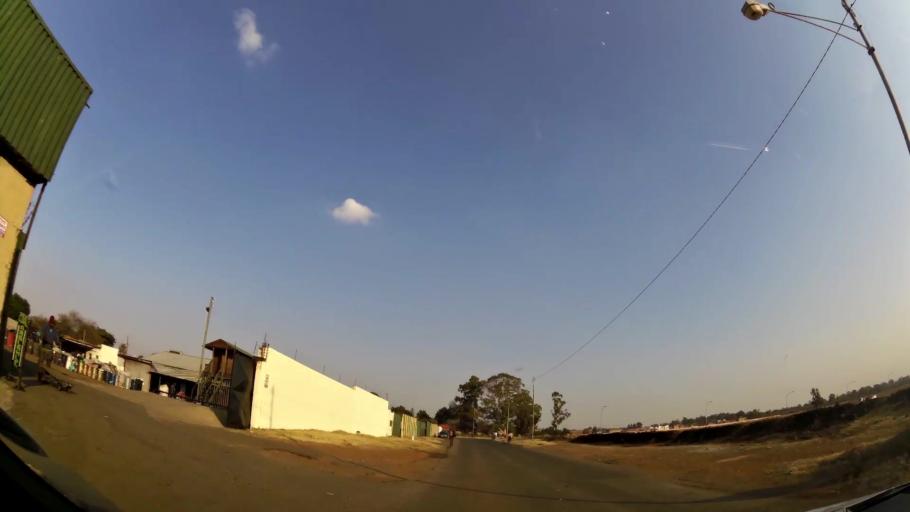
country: ZA
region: Gauteng
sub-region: Ekurhuleni Metropolitan Municipality
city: Springs
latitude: -26.2938
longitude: 28.4406
